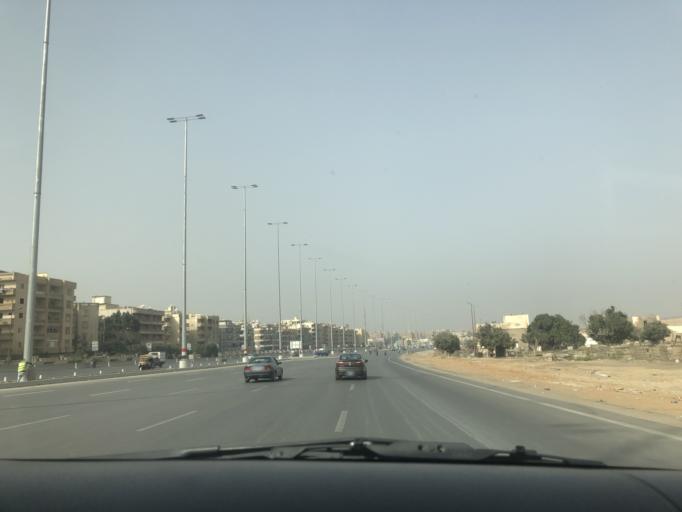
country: EG
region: Al Jizah
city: Al Jizah
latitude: 29.9727
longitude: 31.1096
